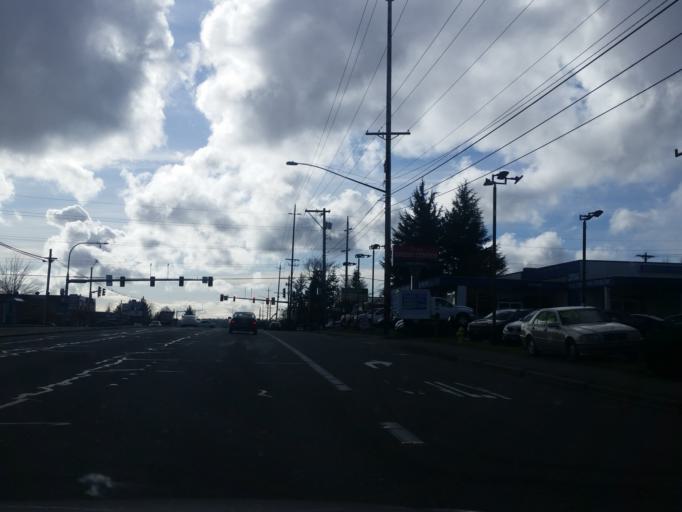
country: US
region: Washington
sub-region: Snohomish County
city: Lynnwood
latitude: 47.8116
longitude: -122.3233
